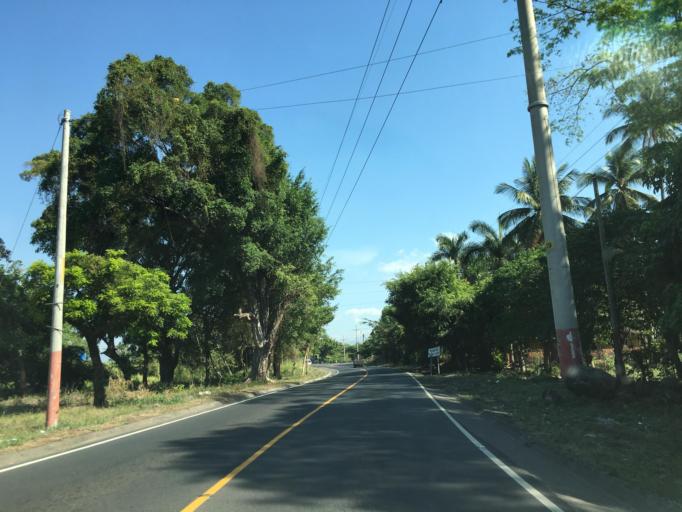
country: GT
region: Escuintla
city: Siquinala
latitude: 14.2929
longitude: -90.9696
